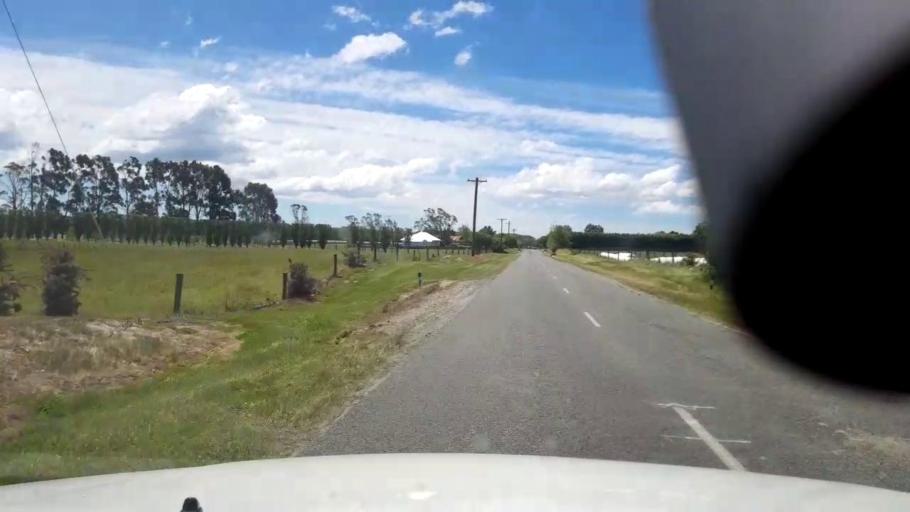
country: NZ
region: Canterbury
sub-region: Timaru District
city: Pleasant Point
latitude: -44.2748
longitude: 171.2527
